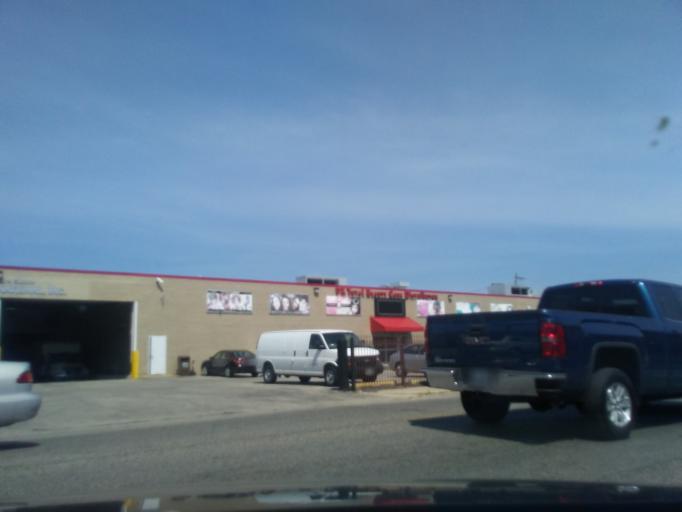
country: US
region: Illinois
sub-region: Cook County
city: Lincolnwood
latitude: 41.9804
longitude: -87.7603
